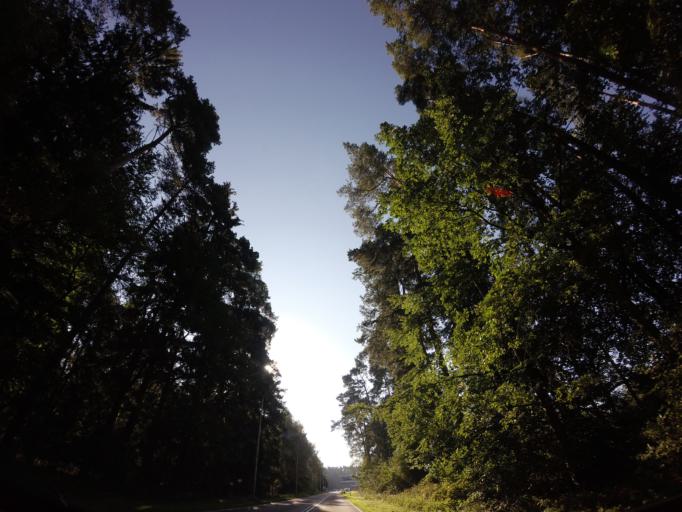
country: PL
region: West Pomeranian Voivodeship
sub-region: Powiat goleniowski
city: Goleniow
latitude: 53.5955
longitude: 14.8923
